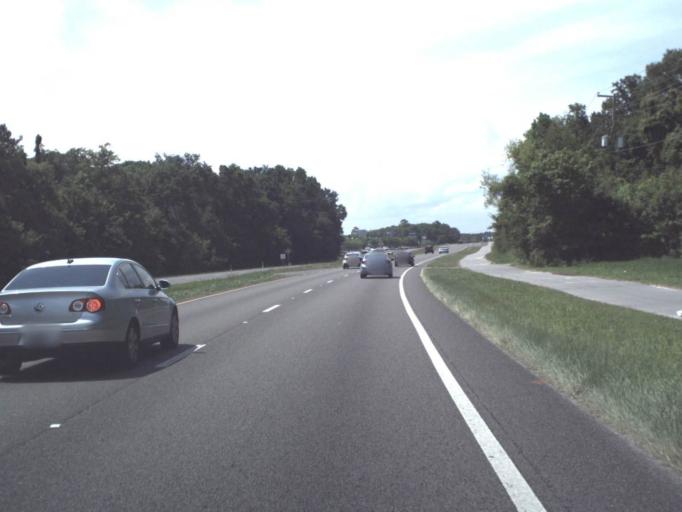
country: US
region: Florida
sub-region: Clay County
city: Green Cove Springs
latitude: 30.0115
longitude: -81.6991
